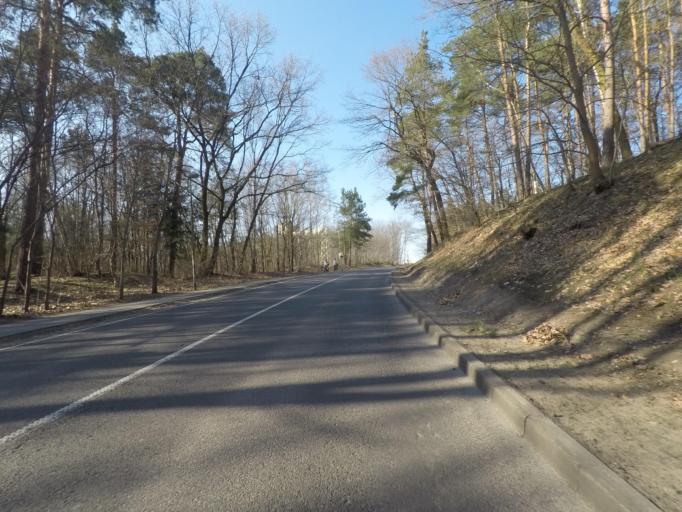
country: DE
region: Brandenburg
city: Eberswalde
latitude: 52.8451
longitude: 13.7904
